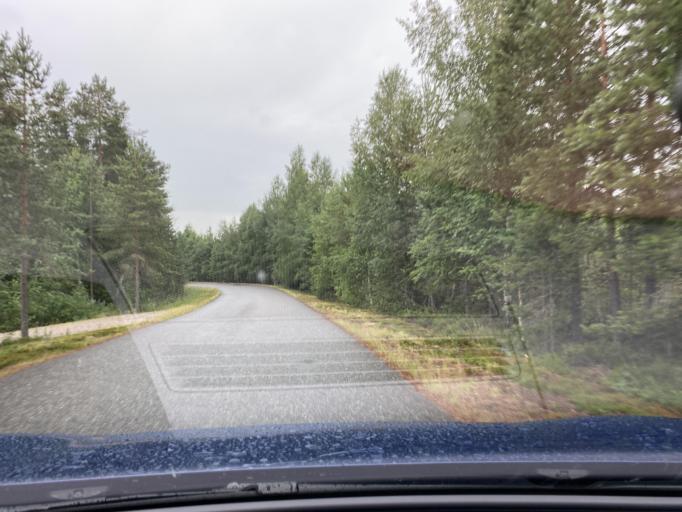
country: FI
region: Central Ostrobothnia
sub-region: Kaustinen
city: Halsua
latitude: 63.4196
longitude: 23.9757
